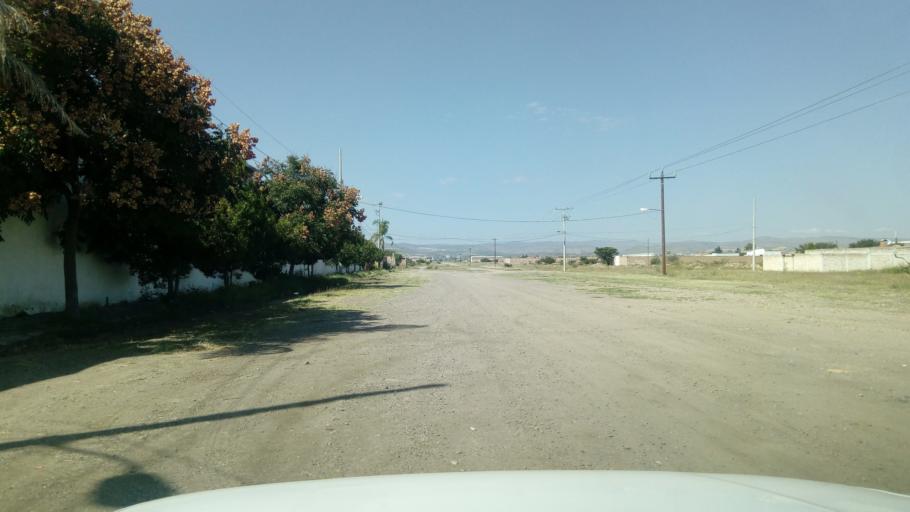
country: MX
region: Durango
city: Victoria de Durango
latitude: 23.9832
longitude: -104.6696
